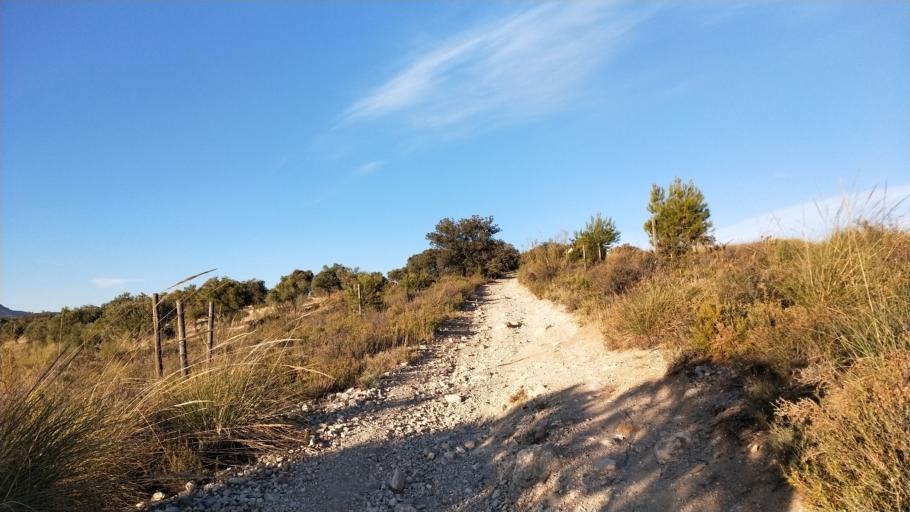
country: ES
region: Andalusia
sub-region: Provincia de Granada
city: Dudar
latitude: 37.1987
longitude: -3.5031
